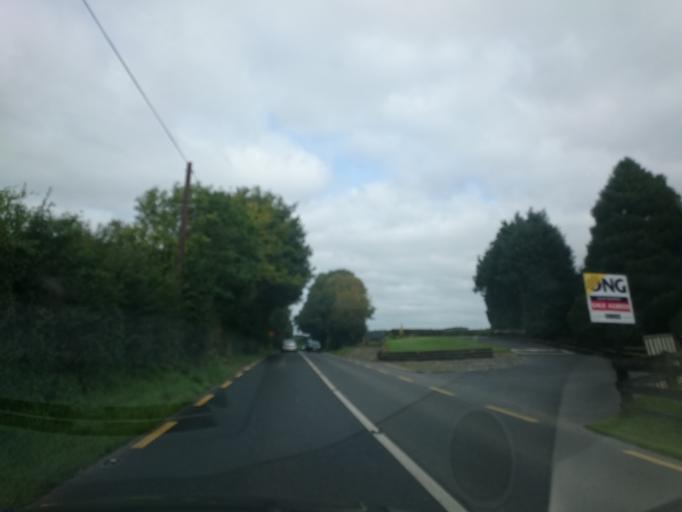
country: IE
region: Leinster
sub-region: Kilkenny
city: Kilkenny
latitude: 52.6824
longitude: -7.2547
